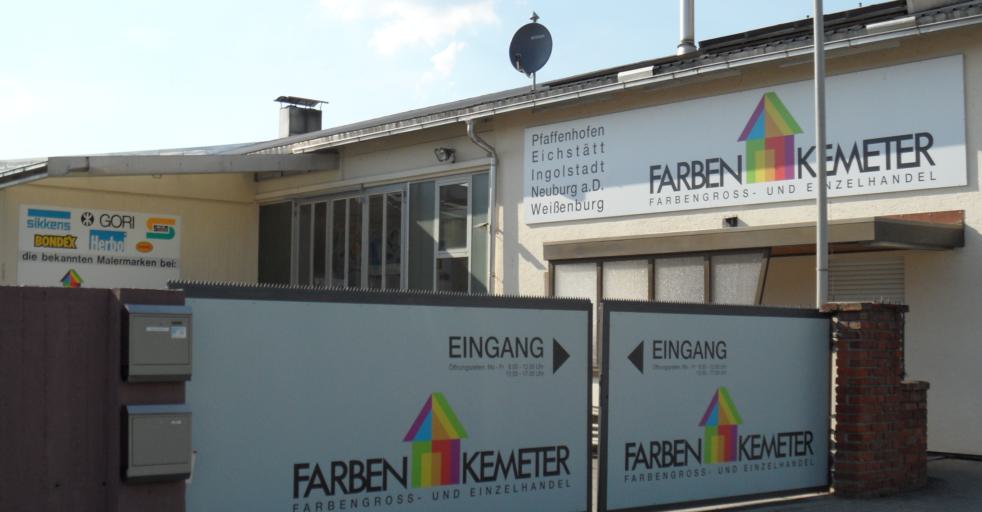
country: DE
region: Bavaria
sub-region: Upper Bavaria
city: Pfaffenhofen an der Ilm
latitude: 48.5337
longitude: 11.5150
